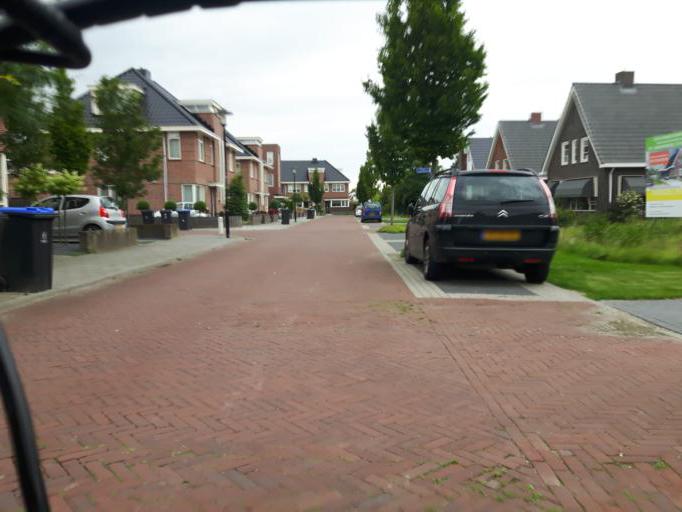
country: NL
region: Zeeland
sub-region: Gemeente Goes
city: Goes
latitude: 51.4956
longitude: 3.9096
